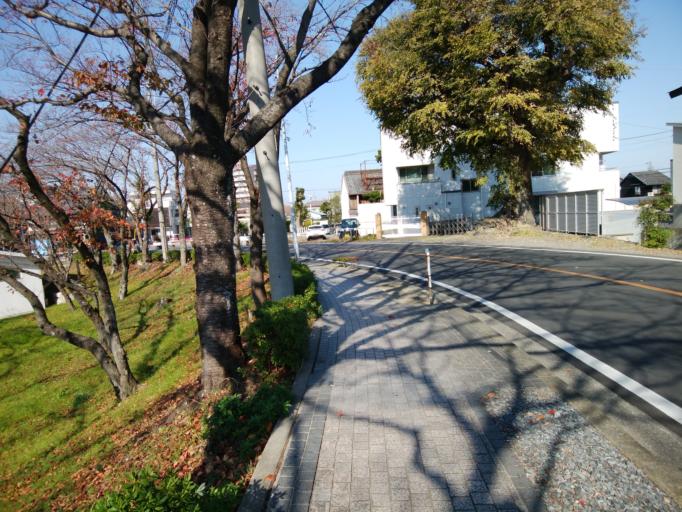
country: JP
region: Aichi
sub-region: Tsushima-shi
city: Tsushima
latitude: 35.1766
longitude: 136.7225
